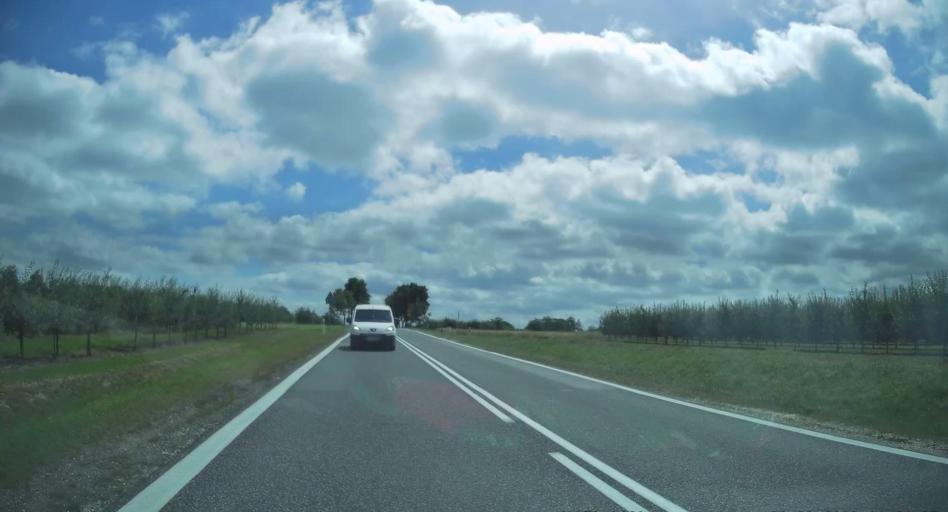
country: PL
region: Swietokrzyskie
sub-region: Powiat sandomierski
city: Loniow
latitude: 50.5784
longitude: 21.4991
